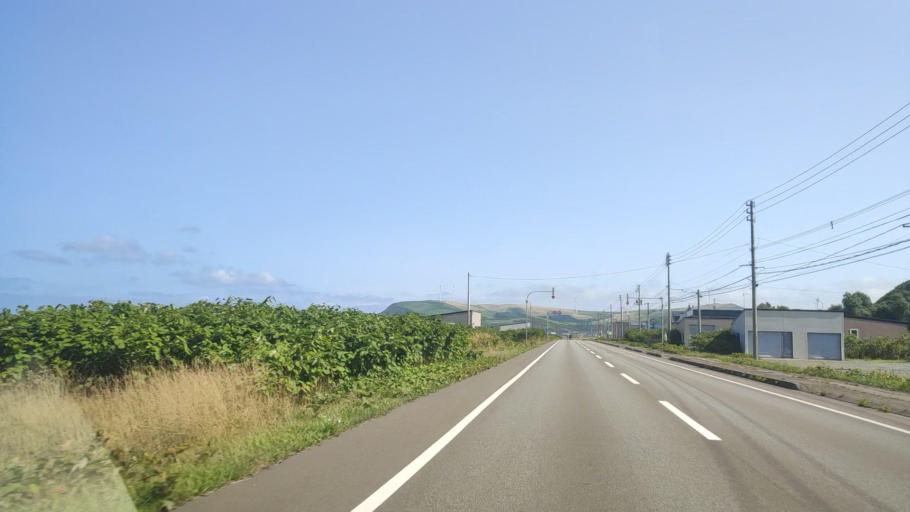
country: JP
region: Hokkaido
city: Makubetsu
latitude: 45.4456
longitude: 141.8686
